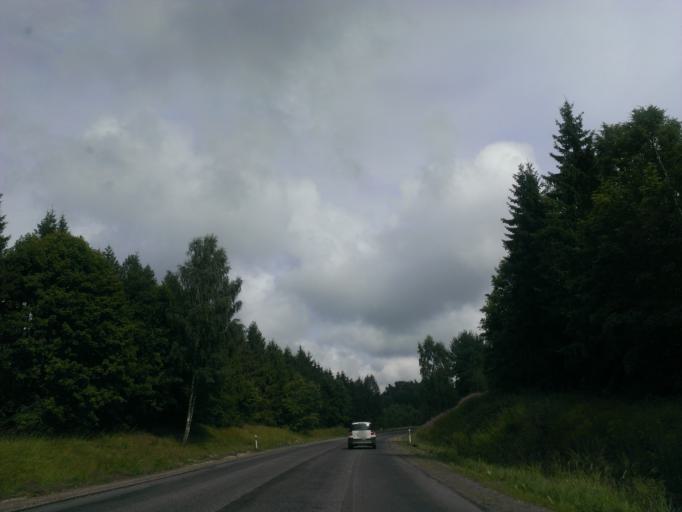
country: LV
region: Ligatne
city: Ligatne
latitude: 57.2038
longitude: 25.1338
